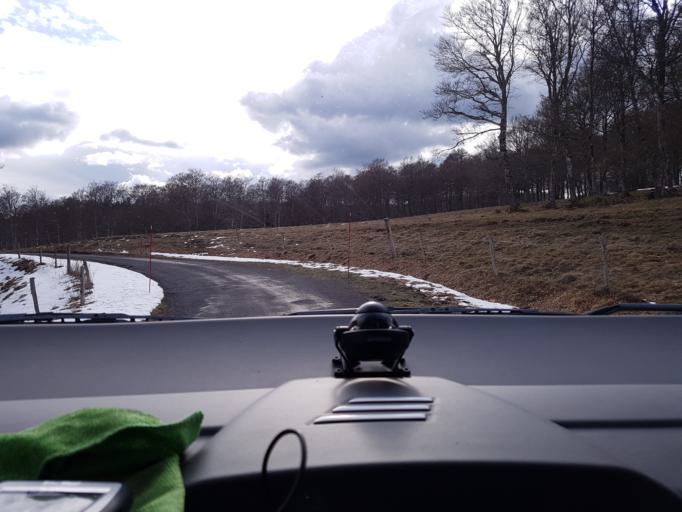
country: FR
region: Midi-Pyrenees
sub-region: Departement de l'Aveyron
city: Laguiole
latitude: 44.6546
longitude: 2.9489
